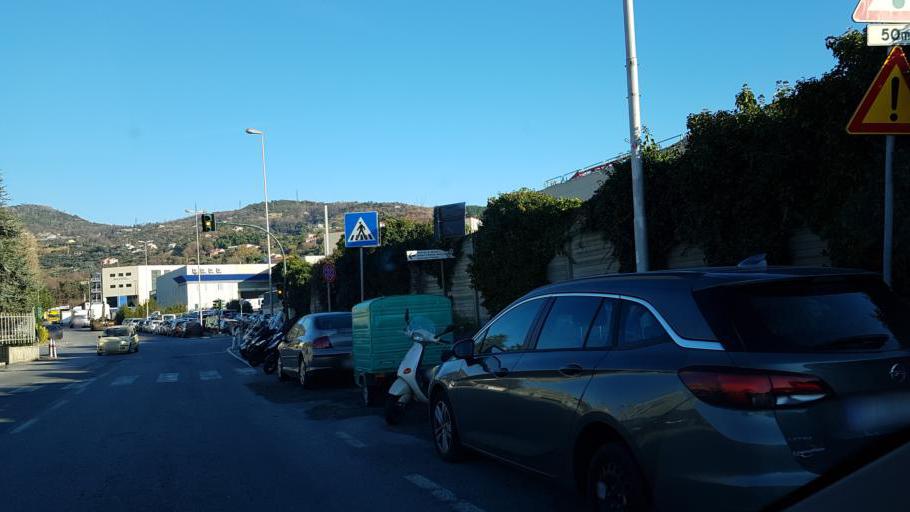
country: IT
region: Liguria
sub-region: Provincia di Savona
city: Savona
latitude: 44.3005
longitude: 8.4554
